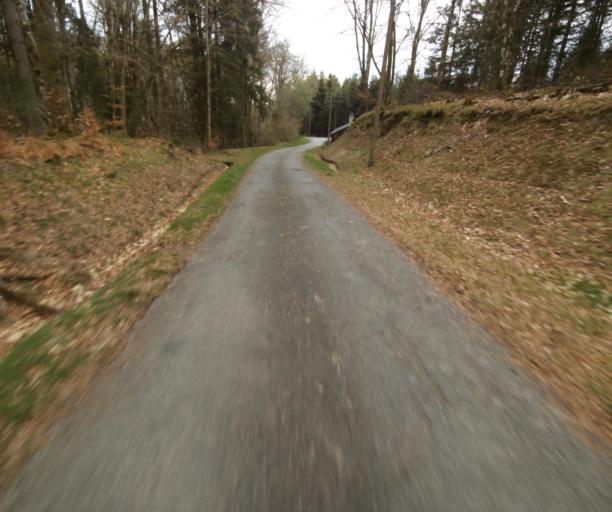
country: FR
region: Limousin
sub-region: Departement de la Correze
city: Argentat
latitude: 45.2214
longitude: 1.9657
